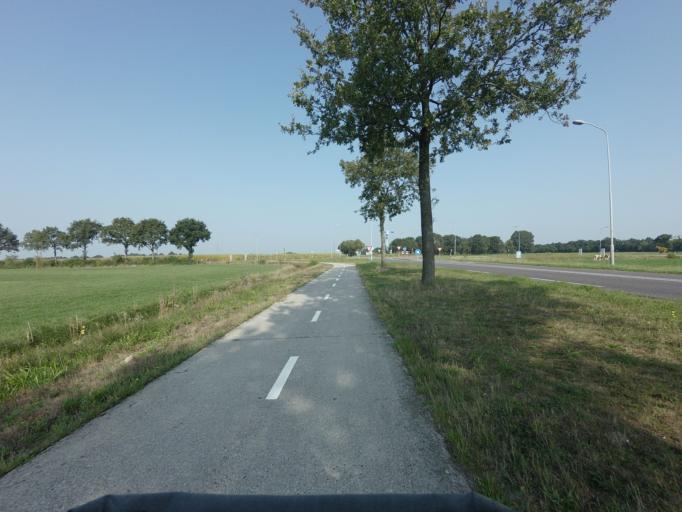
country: NL
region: Drenthe
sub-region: Gemeente Tynaarlo
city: Vries
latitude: 53.1110
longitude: 6.5184
